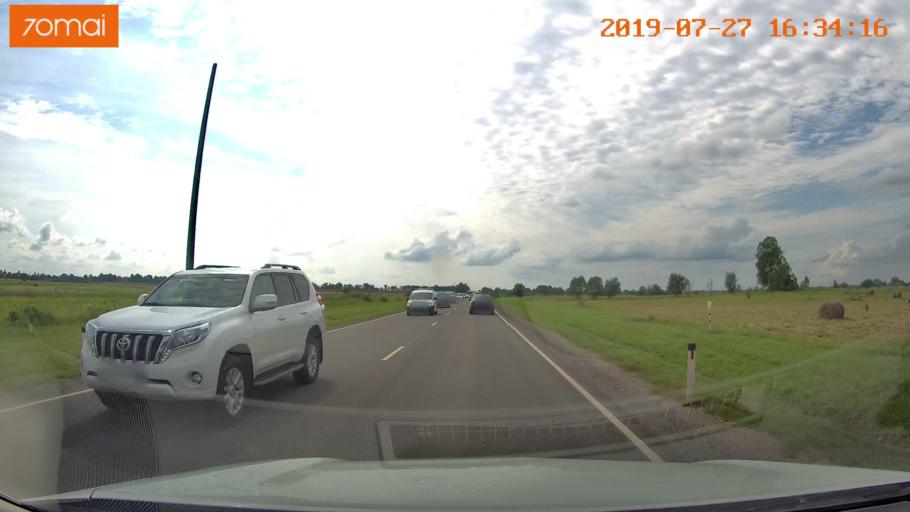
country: RU
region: Kaliningrad
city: Gvardeysk
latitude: 54.6502
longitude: 21.3293
